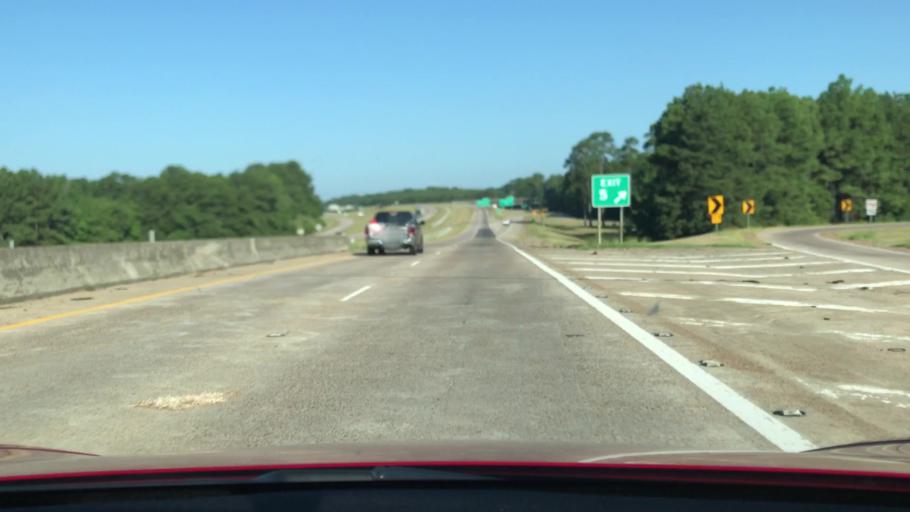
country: US
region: Louisiana
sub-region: Bossier Parish
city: Bossier City
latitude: 32.4160
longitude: -93.7896
